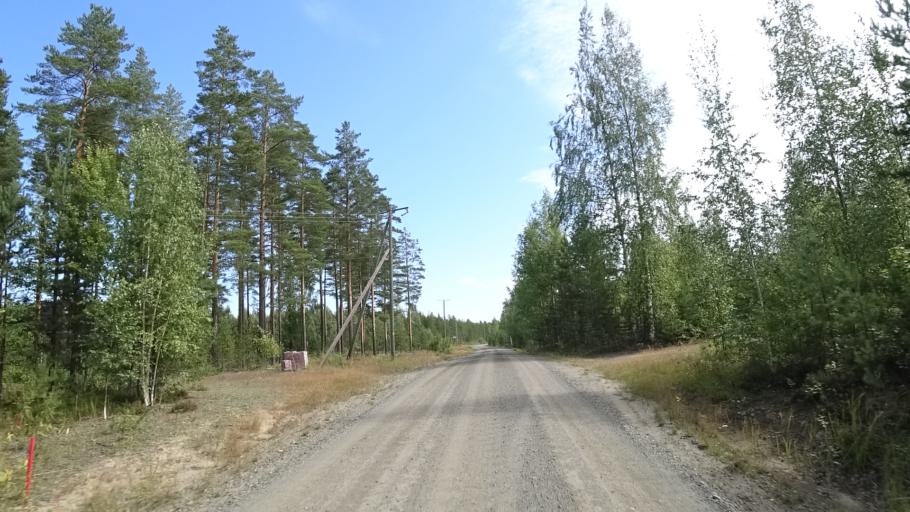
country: FI
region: North Karelia
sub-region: Joensuu
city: Pyhaeselkae
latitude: 62.3733
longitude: 29.8282
